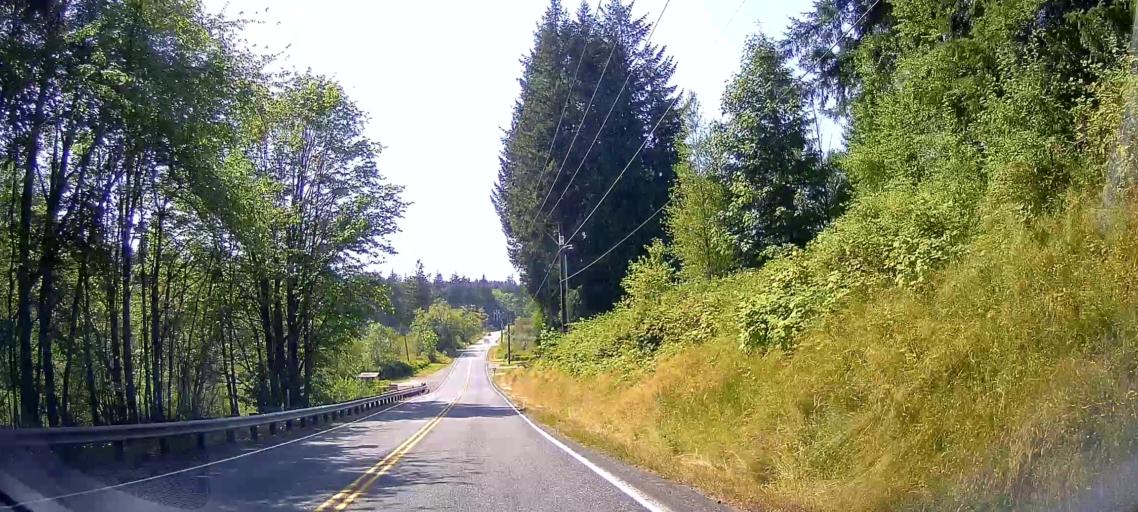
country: US
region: Washington
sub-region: Snohomish County
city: Bryant
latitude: 48.3269
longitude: -122.1467
